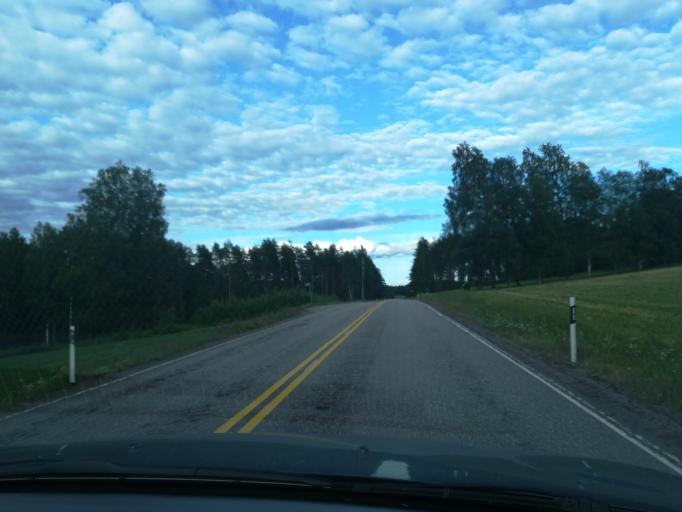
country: FI
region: Southern Savonia
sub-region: Mikkeli
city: Puumala
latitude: 61.5012
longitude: 27.8428
